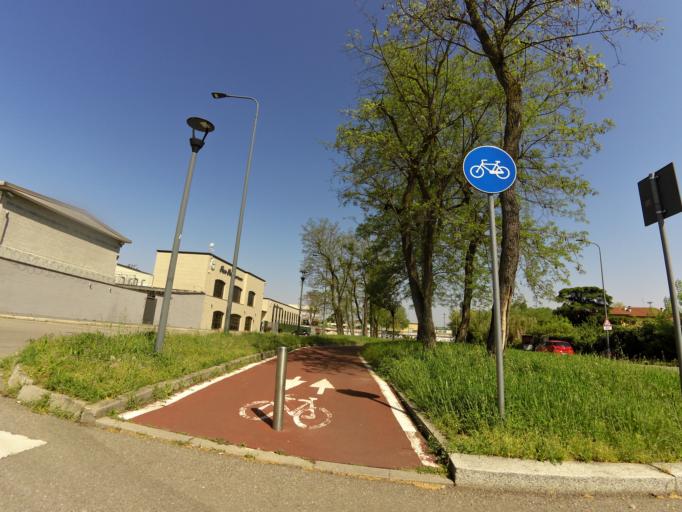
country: IT
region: Lombardy
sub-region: Citta metropolitana di Milano
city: Novegro-Tregarezzo-San Felice
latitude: 45.4704
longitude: 9.2617
